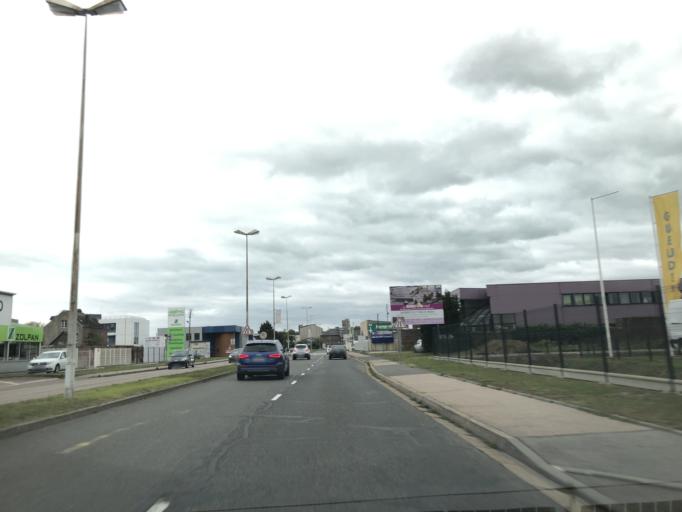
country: FR
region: Haute-Normandie
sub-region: Departement de la Seine-Maritime
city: Rouxmesnil-Bouteilles
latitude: 49.9190
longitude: 1.0861
